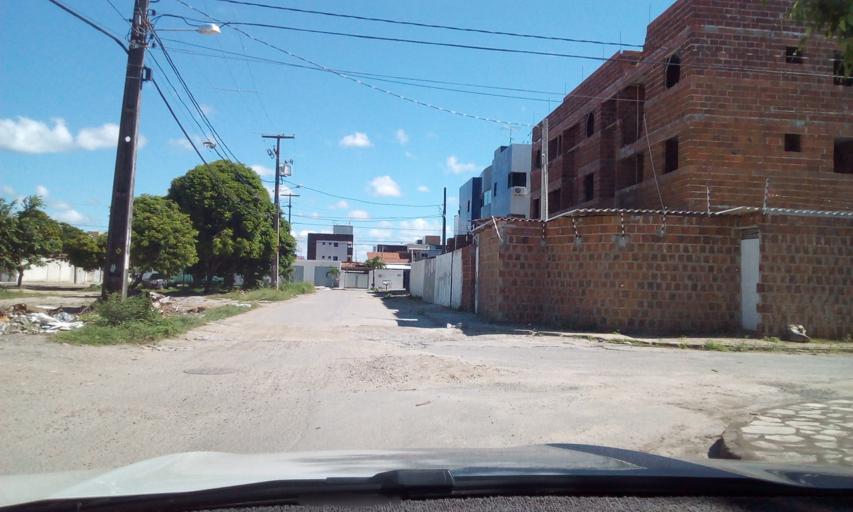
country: BR
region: Paraiba
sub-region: Joao Pessoa
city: Joao Pessoa
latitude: -7.1742
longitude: -34.8577
